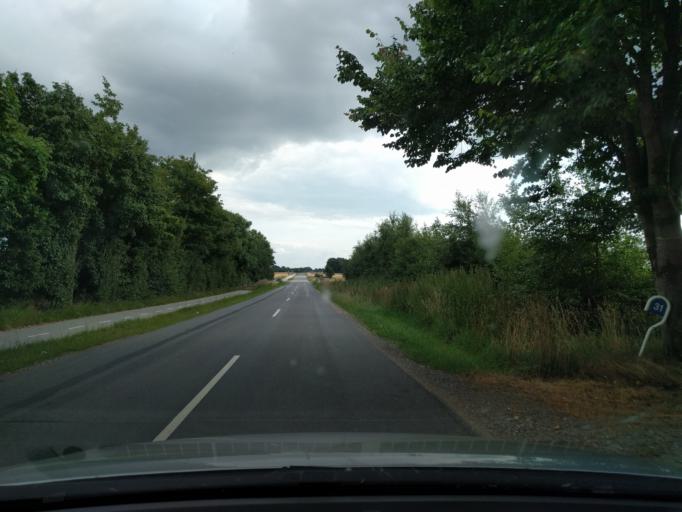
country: DK
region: Central Jutland
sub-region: Herning Kommune
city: Snejbjerg
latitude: 56.1064
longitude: 8.9083
